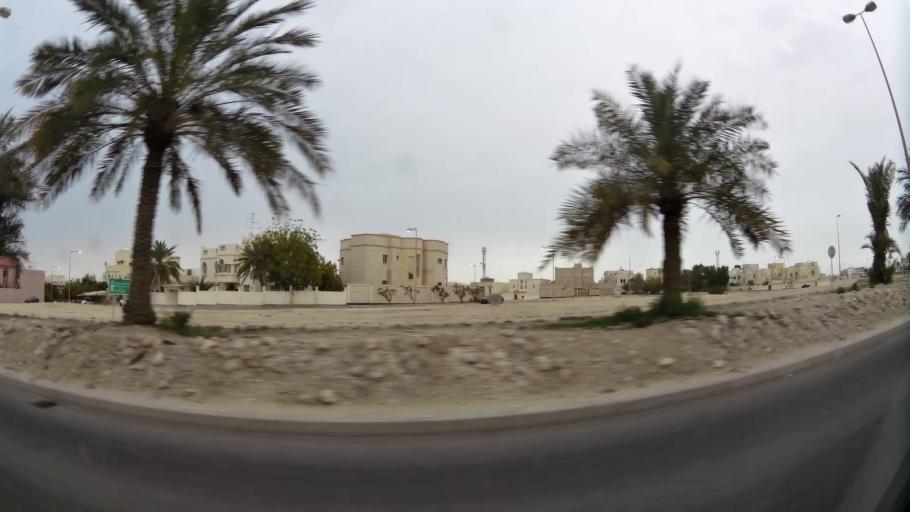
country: BH
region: Central Governorate
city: Madinat Hamad
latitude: 26.1041
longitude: 50.5040
